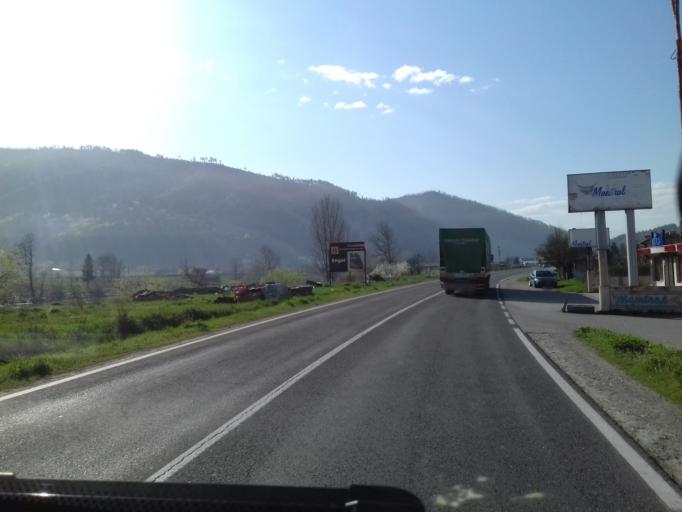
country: BA
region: Federation of Bosnia and Herzegovina
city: Maglaj
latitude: 44.5977
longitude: 18.0895
